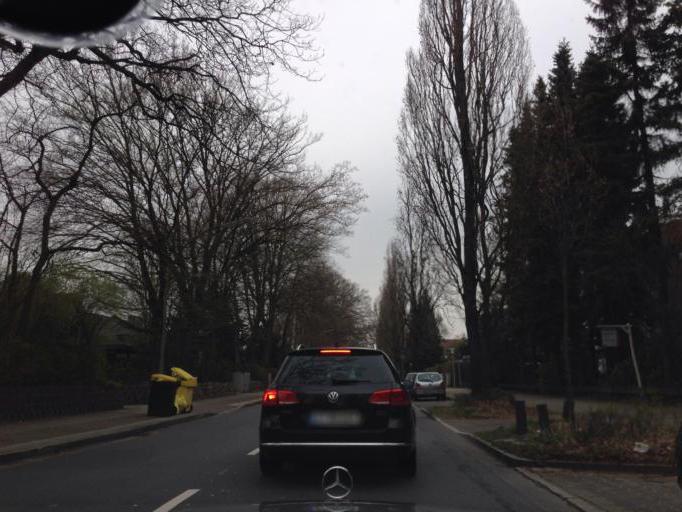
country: DE
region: Hamburg
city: Sasel
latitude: 53.6511
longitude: 10.1159
